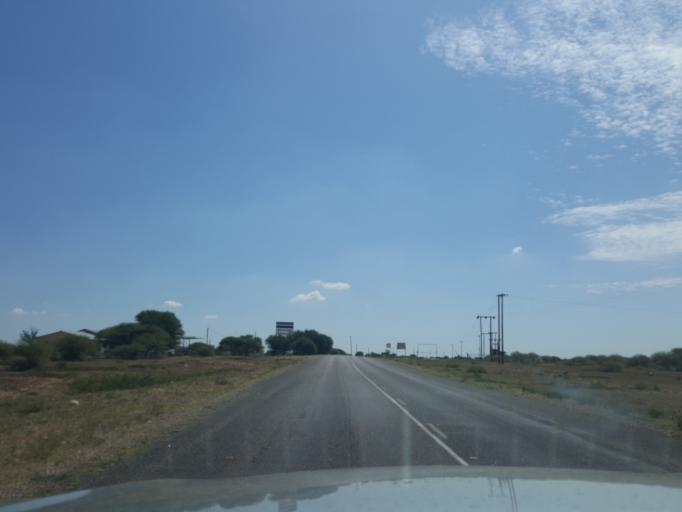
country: BW
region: Kweneng
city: Letlhakeng
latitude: -24.1170
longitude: 25.0442
